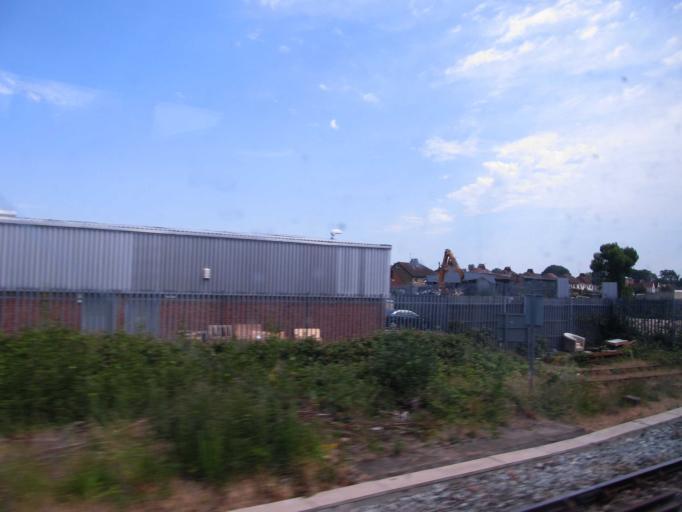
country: GB
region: England
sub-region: Slough
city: Slough
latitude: 51.5168
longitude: -0.6137
